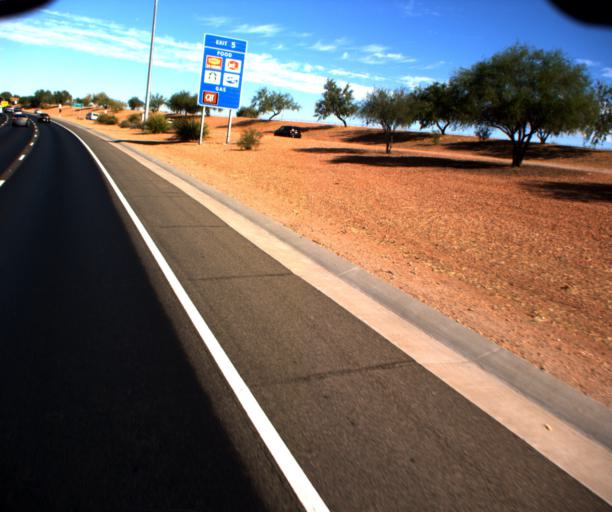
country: US
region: Arizona
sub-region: Maricopa County
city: Tolleson
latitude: 33.4956
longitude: -112.2642
